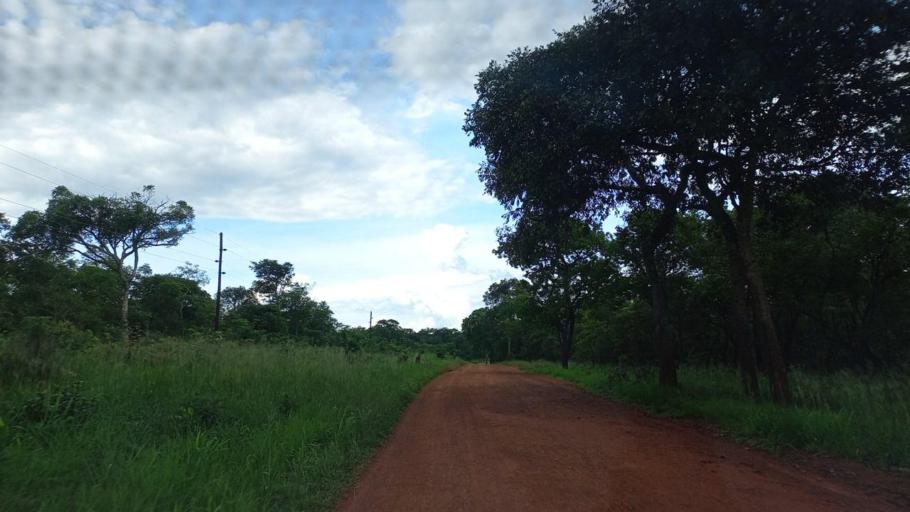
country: ZM
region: North-Western
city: Mwinilunga
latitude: -11.7854
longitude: 24.3734
